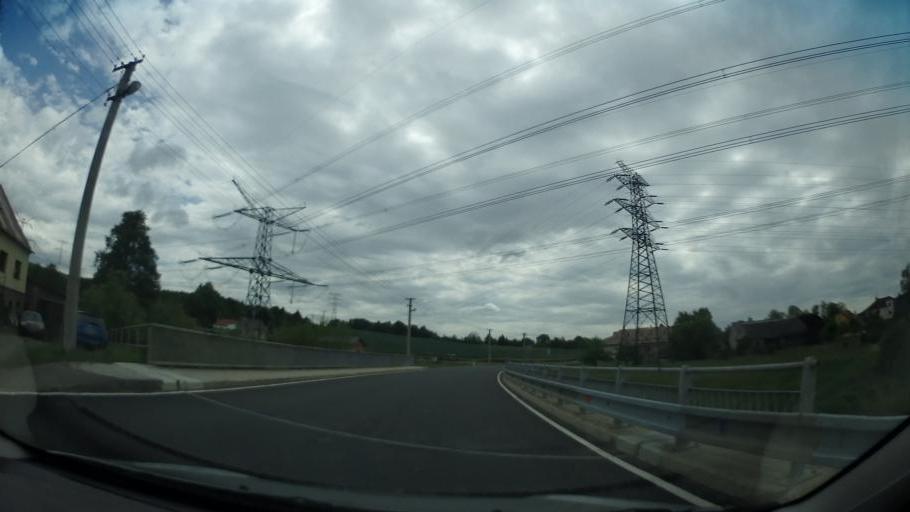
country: CZ
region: Pardubicky
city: Kuncina
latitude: 49.8476
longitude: 16.6972
